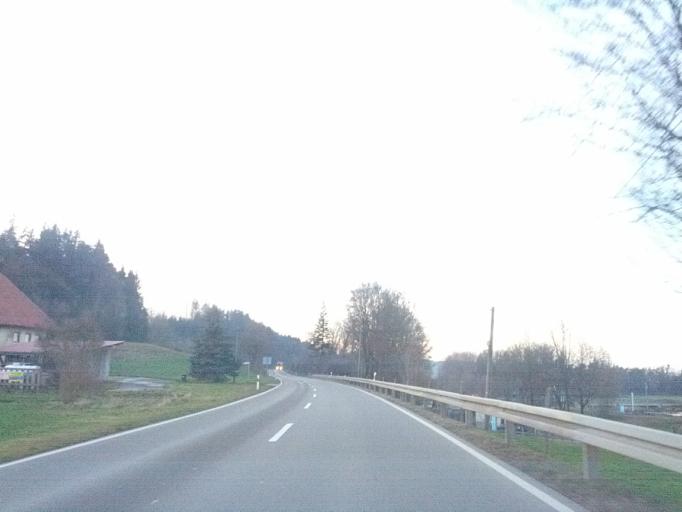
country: DE
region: Bavaria
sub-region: Swabia
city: Lautrach
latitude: 47.9176
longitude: 10.1114
